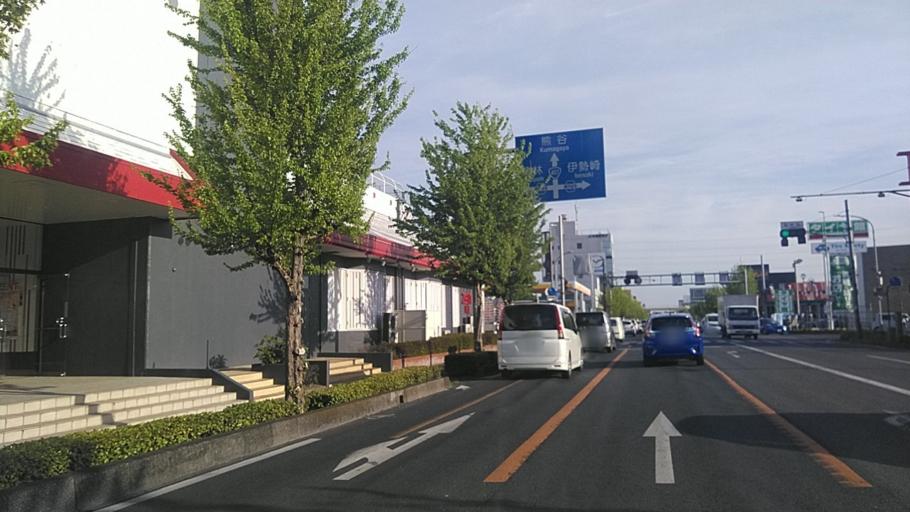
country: JP
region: Gunma
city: Ota
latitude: 36.2858
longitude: 139.3768
